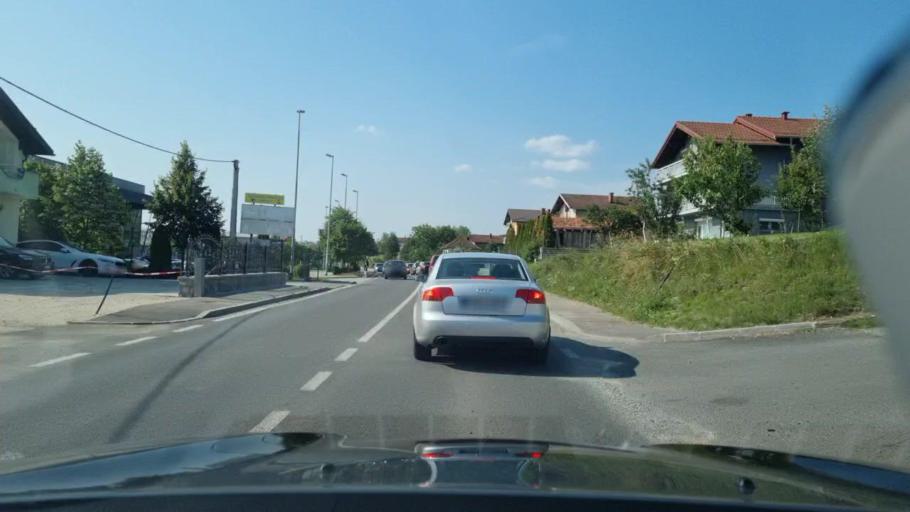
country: BA
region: Federation of Bosnia and Herzegovina
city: Cazin
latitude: 44.9699
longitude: 15.8986
